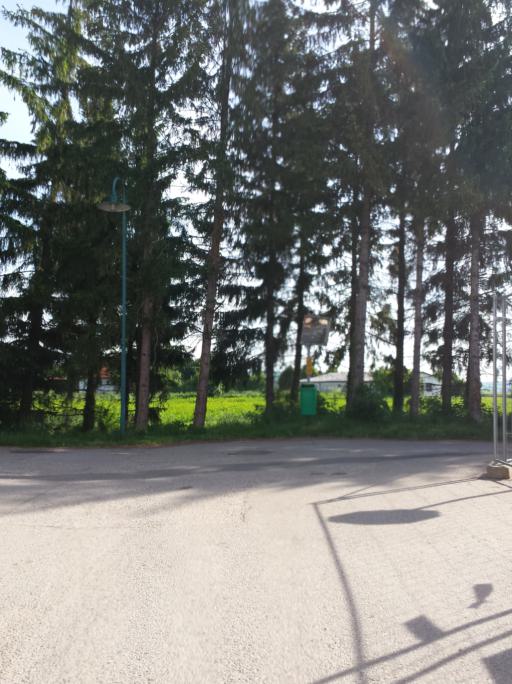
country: AT
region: Lower Austria
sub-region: Politischer Bezirk Hollabrunn
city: Wullersdorf
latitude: 48.6306
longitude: 16.1044
